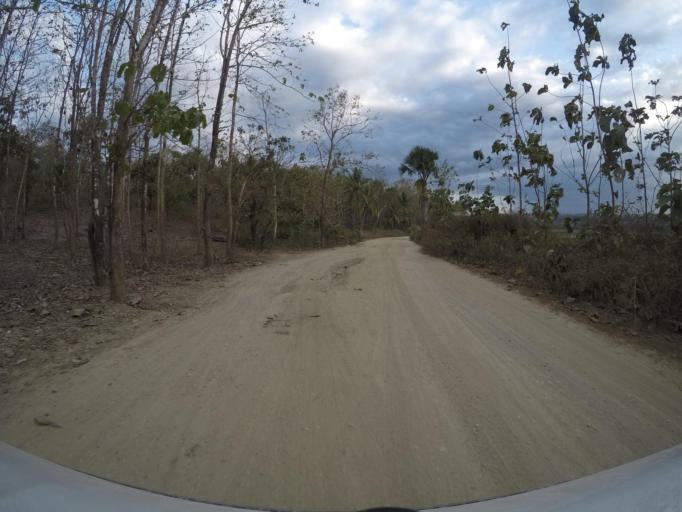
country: TL
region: Bobonaro
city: Maliana
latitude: -8.8881
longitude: 125.2093
